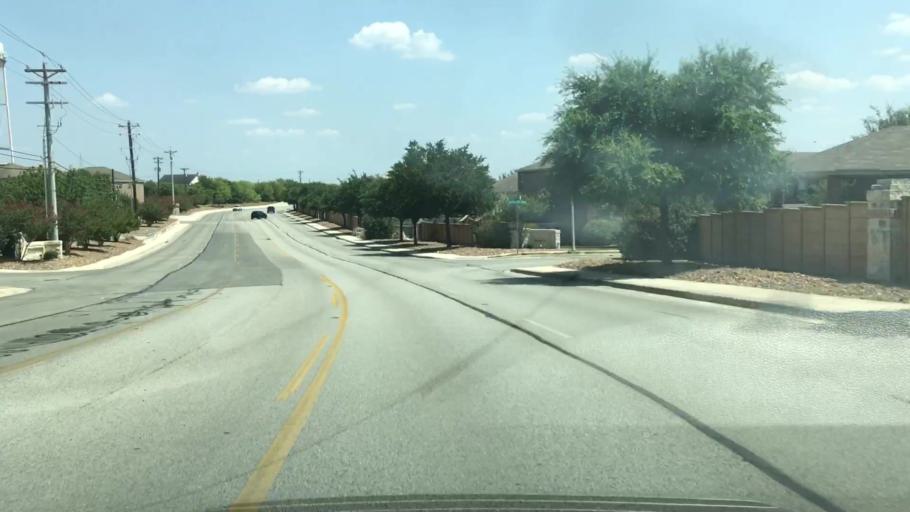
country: US
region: Texas
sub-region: Guadalupe County
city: Northcliff
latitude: 29.5983
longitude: -98.2589
